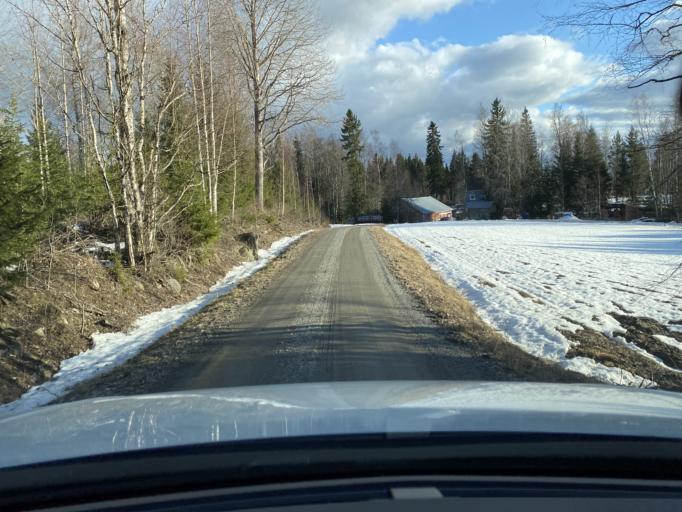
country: FI
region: Pirkanmaa
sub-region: Lounais-Pirkanmaa
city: Mouhijaervi
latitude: 61.4608
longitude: 22.9587
